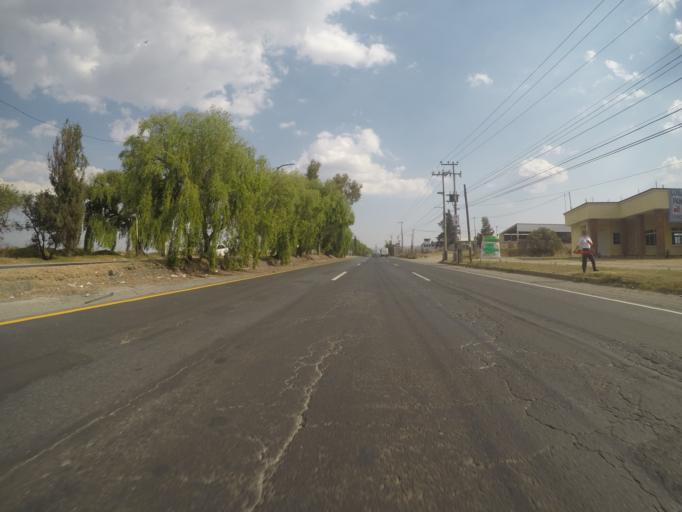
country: MX
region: Morelos
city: San Miguel Totocuitlapilco
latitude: 19.2228
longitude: -99.5933
